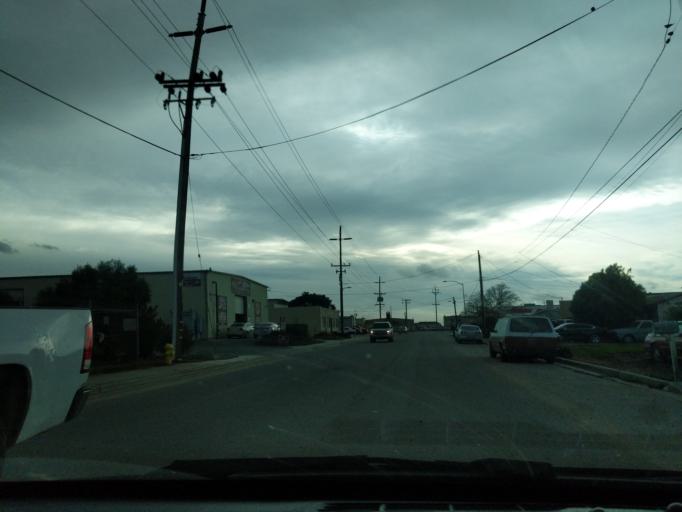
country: US
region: California
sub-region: Monterey County
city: Soledad
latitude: 36.4195
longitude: -121.3208
